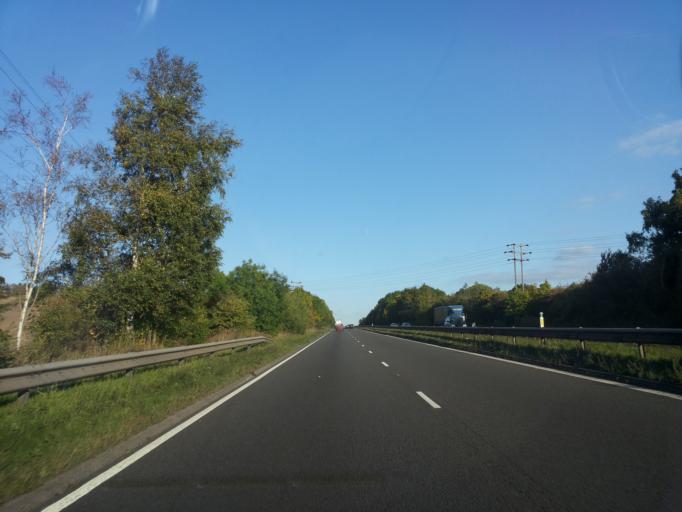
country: GB
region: England
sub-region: Derbyshire
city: Pilsley
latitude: 53.2008
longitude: -1.3550
